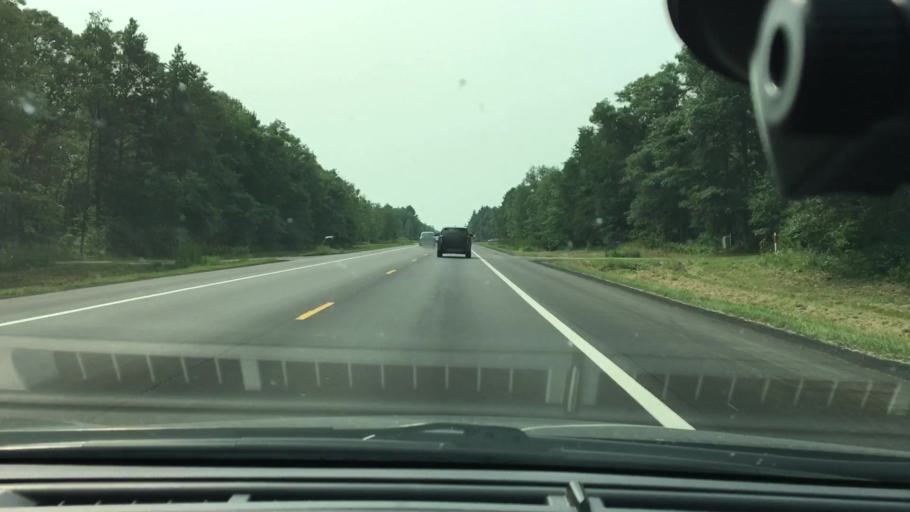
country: US
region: Minnesota
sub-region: Crow Wing County
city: Brainerd
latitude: 46.4537
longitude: -94.1722
